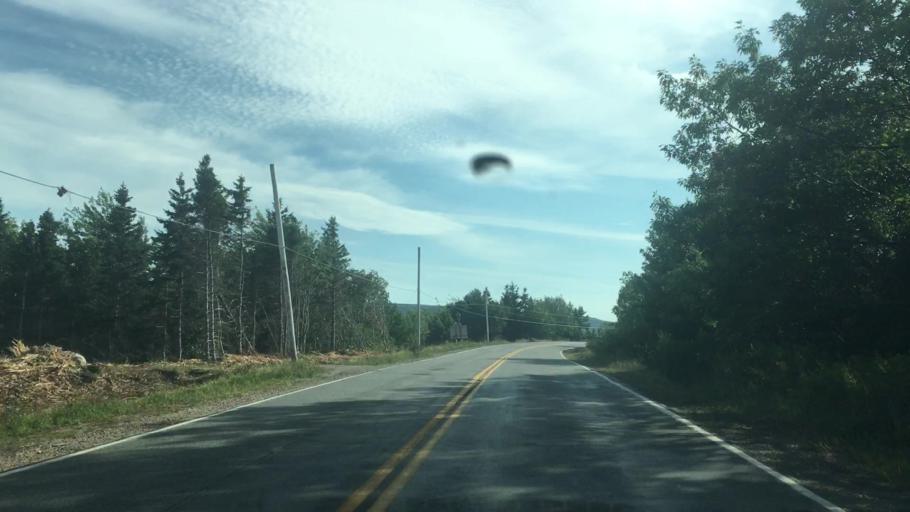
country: CA
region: Nova Scotia
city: Sydney Mines
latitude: 46.8794
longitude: -60.5166
